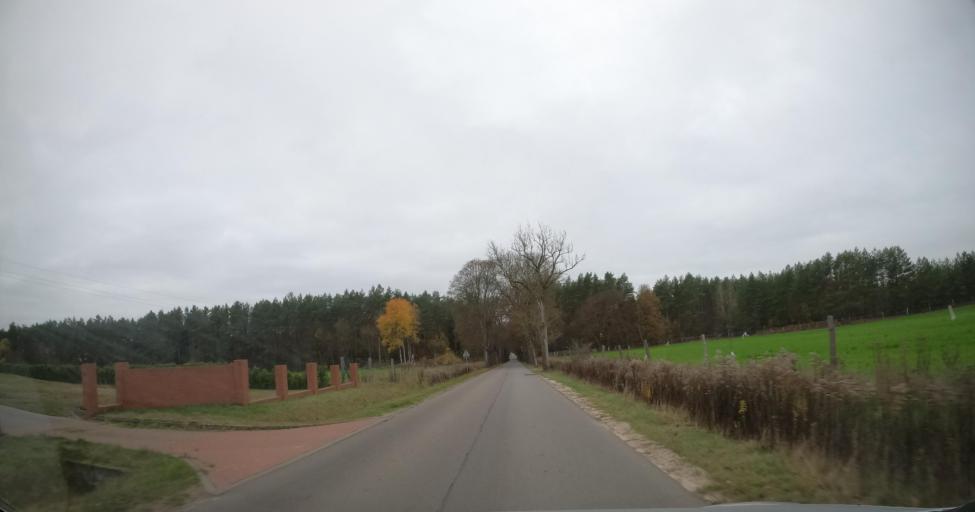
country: PL
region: West Pomeranian Voivodeship
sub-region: Powiat swidwinski
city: Polczyn-Zdroj
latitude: 53.7744
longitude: 16.1591
